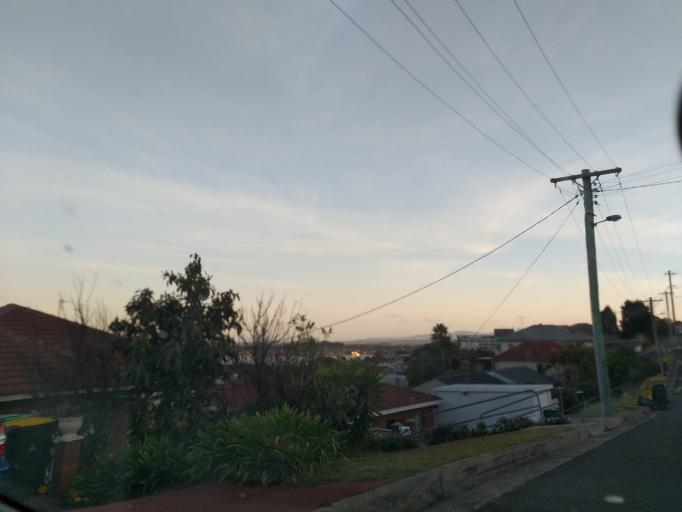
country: AU
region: New South Wales
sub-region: Wollongong
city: Lake Heights
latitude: -34.4812
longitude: 150.8834
